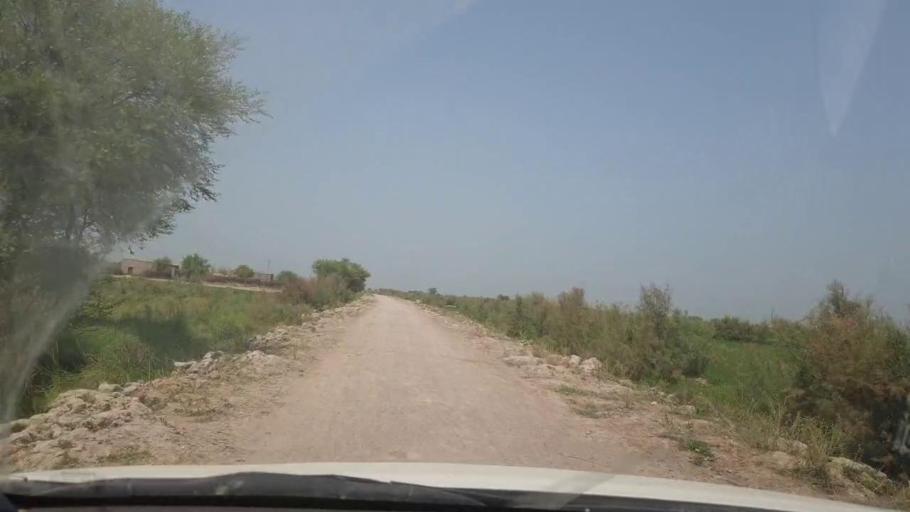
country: PK
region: Sindh
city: Lakhi
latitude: 27.8847
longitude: 68.7427
